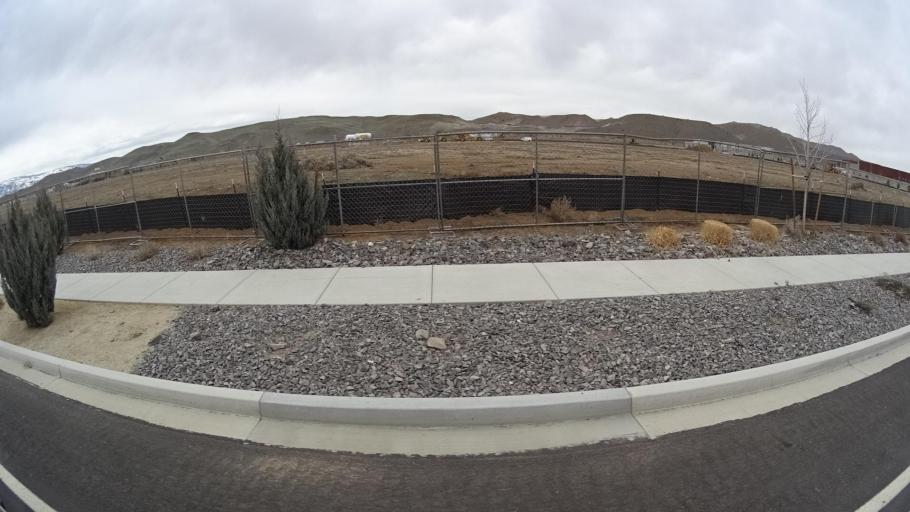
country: US
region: Nevada
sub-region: Washoe County
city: Spanish Springs
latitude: 39.6067
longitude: -119.7204
